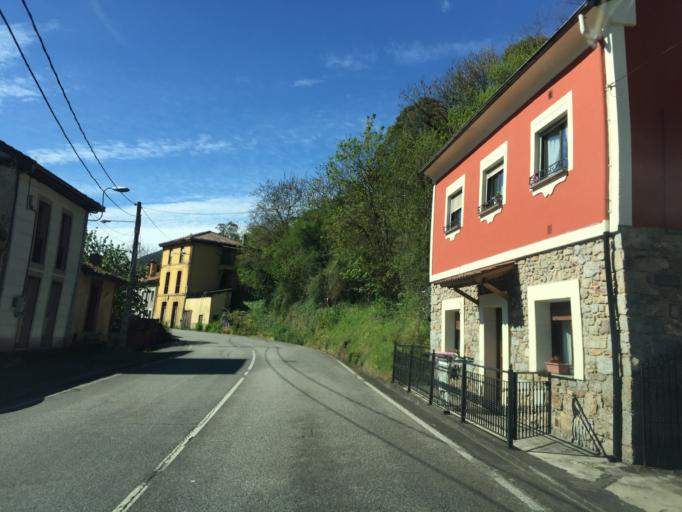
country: ES
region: Asturias
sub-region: Province of Asturias
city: Proaza
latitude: 43.3364
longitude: -5.9863
